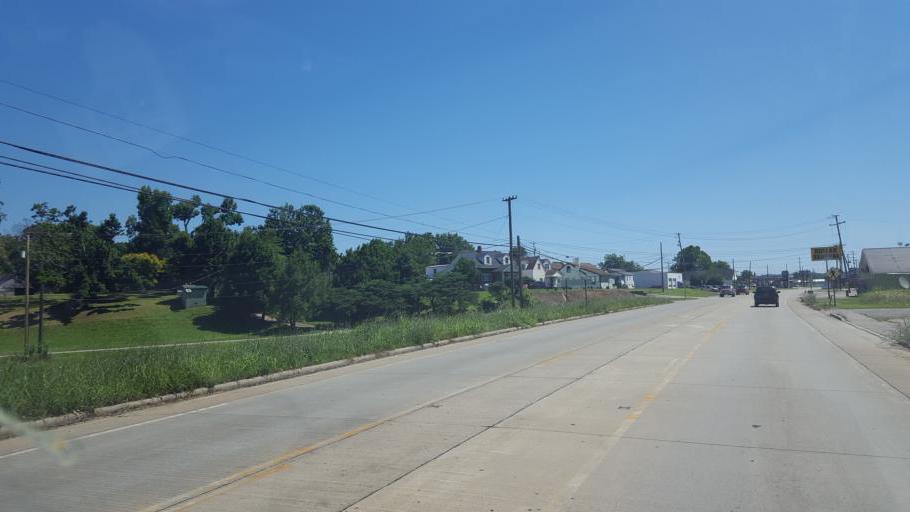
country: US
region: West Virginia
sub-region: Cabell County
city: Pea Ridge
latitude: 38.4404
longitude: -82.3673
